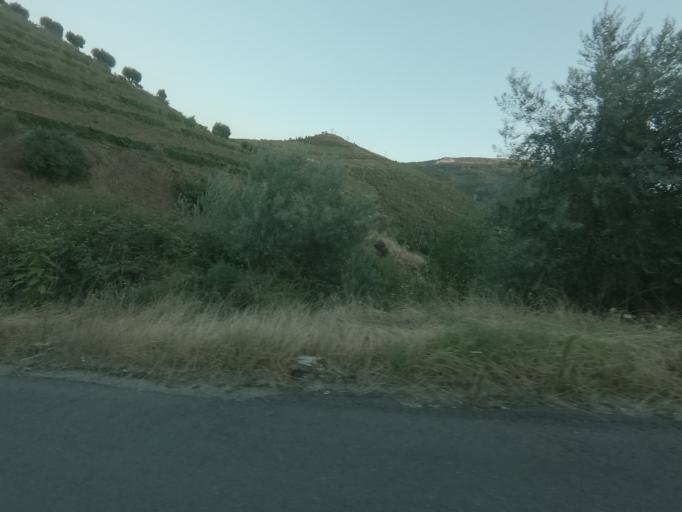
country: PT
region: Vila Real
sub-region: Peso da Regua
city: Peso da Regua
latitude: 41.1490
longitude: -7.7327
